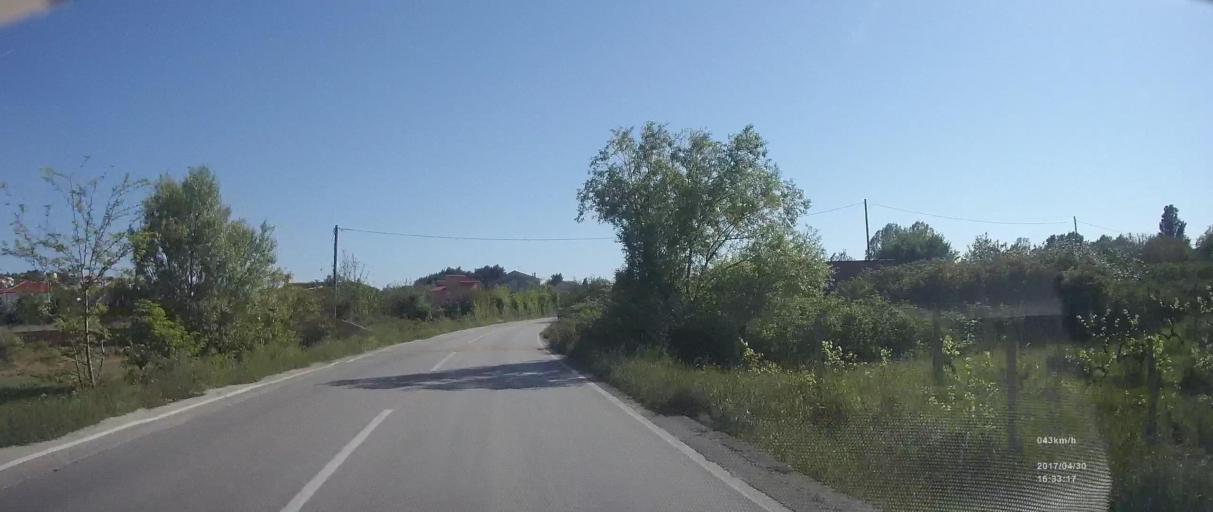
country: HR
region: Splitsko-Dalmatinska
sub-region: Grad Split
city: Stobrec
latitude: 43.5087
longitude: 16.5378
